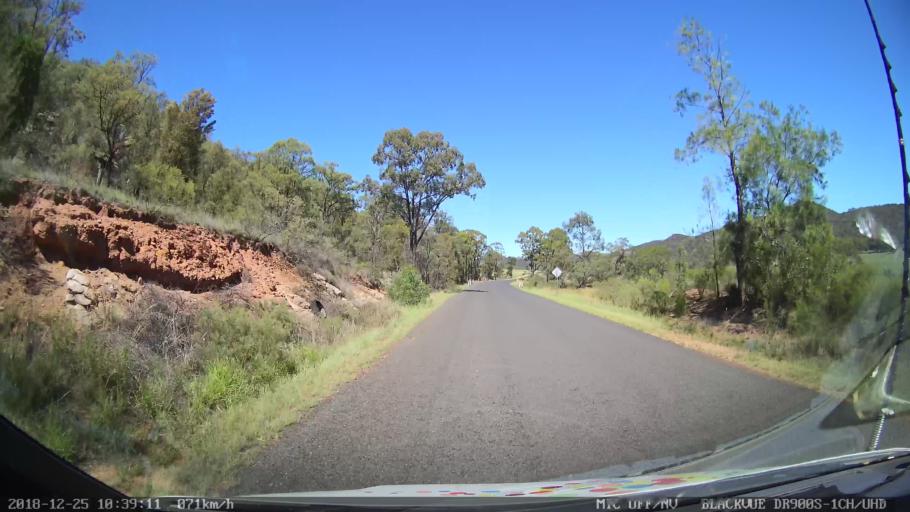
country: AU
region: New South Wales
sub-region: Upper Hunter Shire
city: Merriwa
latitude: -32.4046
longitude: 150.3595
